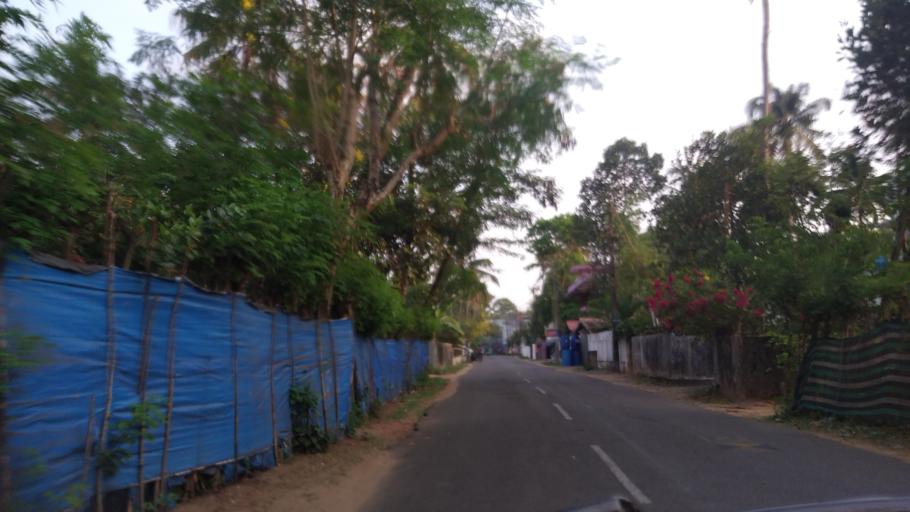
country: IN
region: Kerala
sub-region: Thrissur District
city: Thanniyam
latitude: 10.3541
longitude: 76.1123
